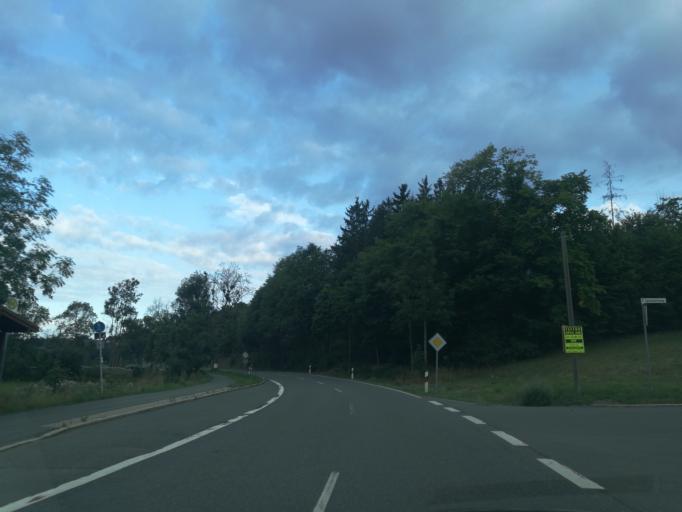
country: DE
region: Bavaria
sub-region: Upper Franconia
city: Dohlau
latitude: 50.2959
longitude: 11.9483
